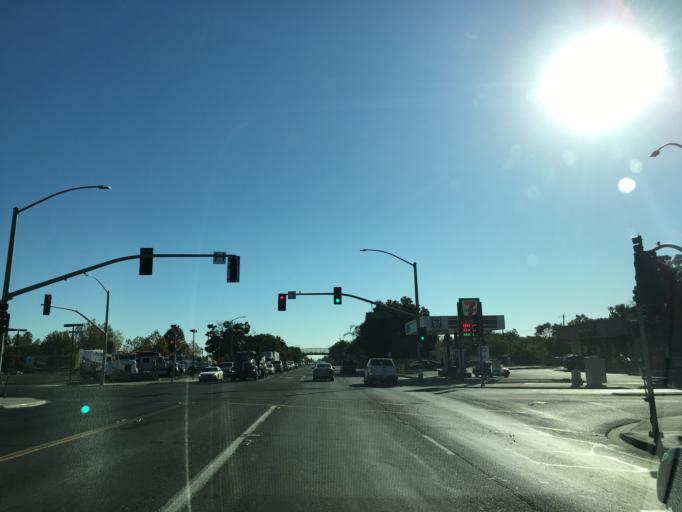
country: US
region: California
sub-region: Merced County
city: Los Banos
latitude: 37.0568
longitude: -120.8514
